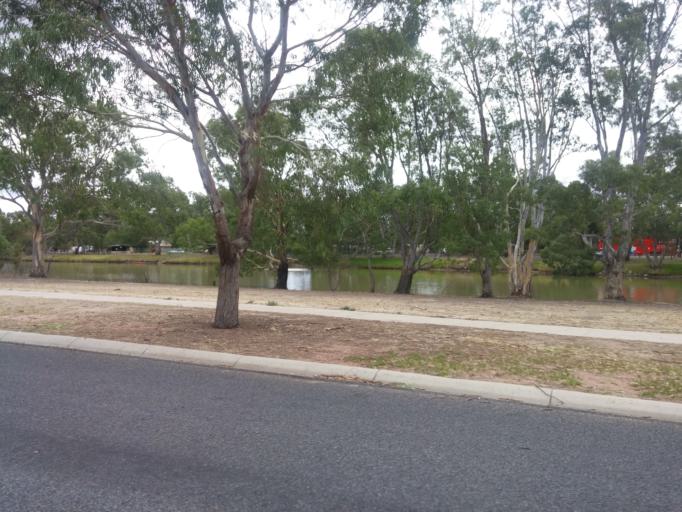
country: AU
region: Victoria
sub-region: Horsham
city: Horsham
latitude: -36.7241
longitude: 142.2013
